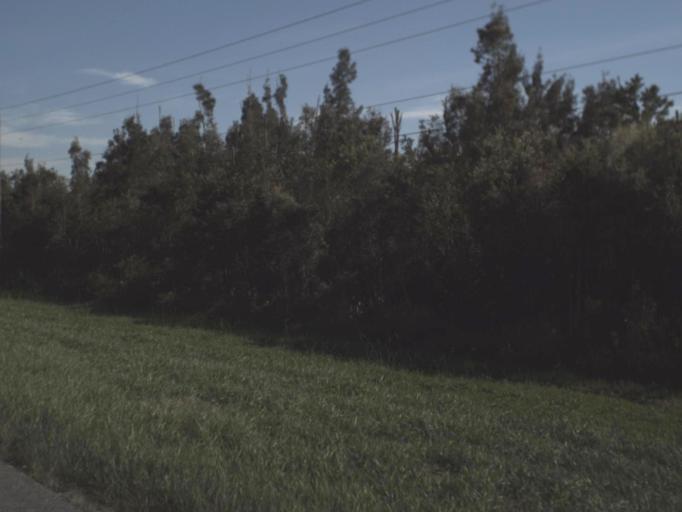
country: US
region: Florida
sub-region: Hendry County
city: Clewiston
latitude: 26.7464
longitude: -80.8926
